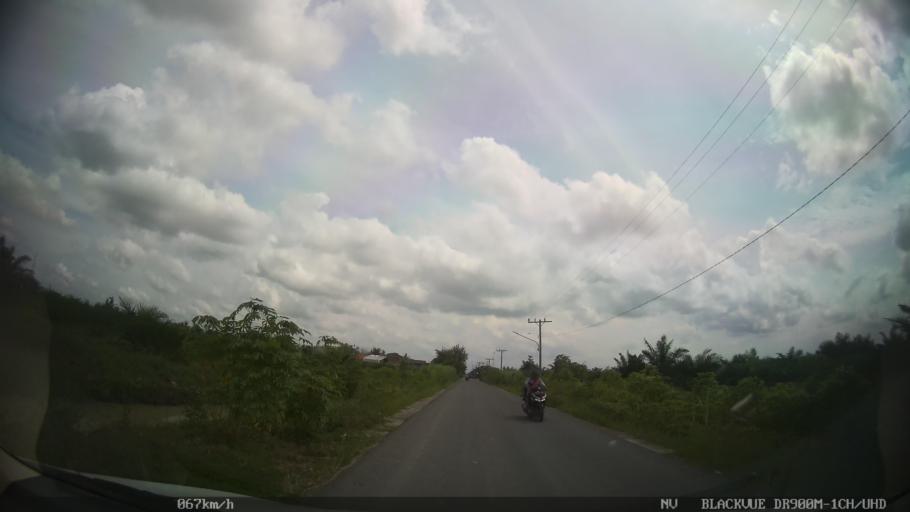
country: ID
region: North Sumatra
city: Percut
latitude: 3.5801
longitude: 98.8408
